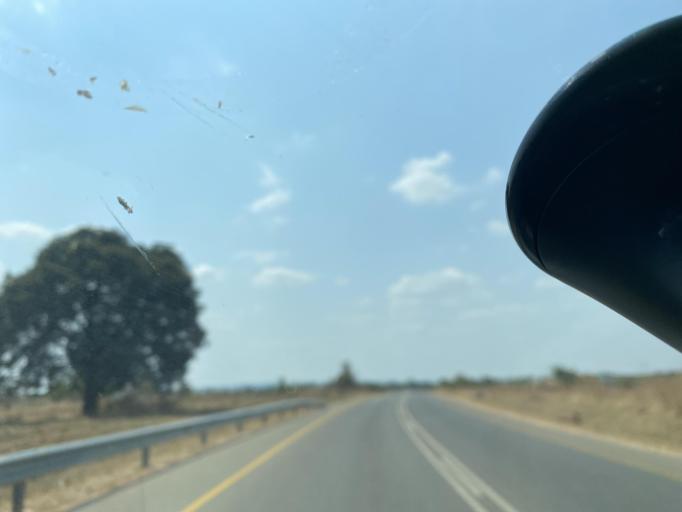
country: ZM
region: Lusaka
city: Chongwe
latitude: -15.5846
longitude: 28.7072
